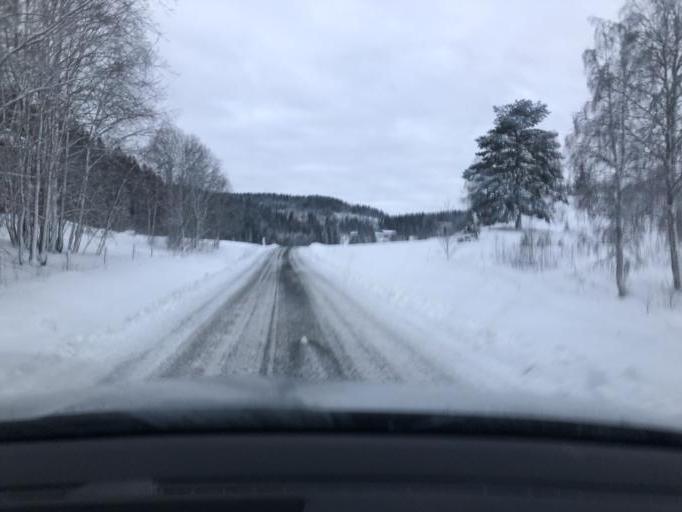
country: SE
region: Vaesternorrland
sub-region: Kramfors Kommun
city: Nordingra
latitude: 62.9096
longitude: 18.2387
